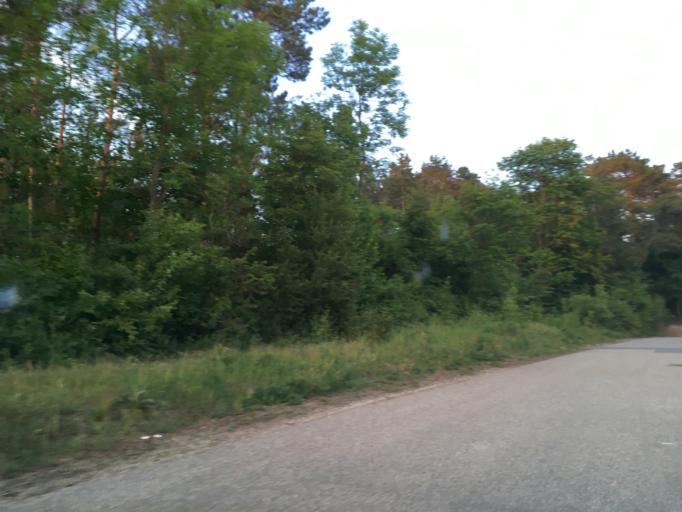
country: AT
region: Lower Austria
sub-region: Politischer Bezirk Korneuburg
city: Stockerau
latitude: 48.3933
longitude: 16.1957
